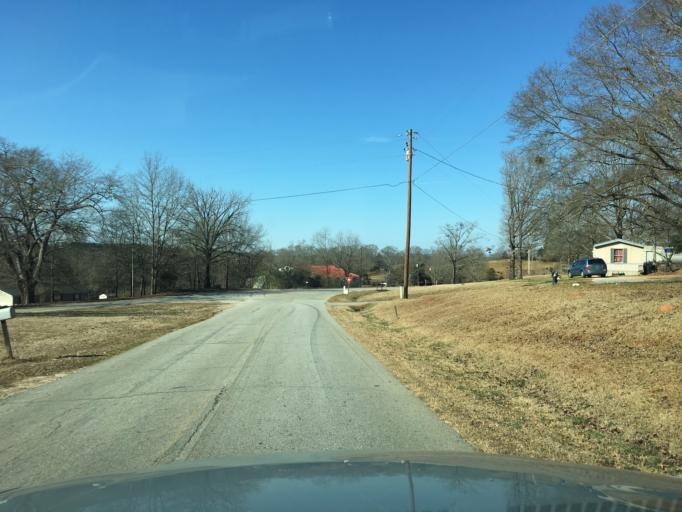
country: US
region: South Carolina
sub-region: Pickens County
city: Arial
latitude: 34.8732
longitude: -82.6606
